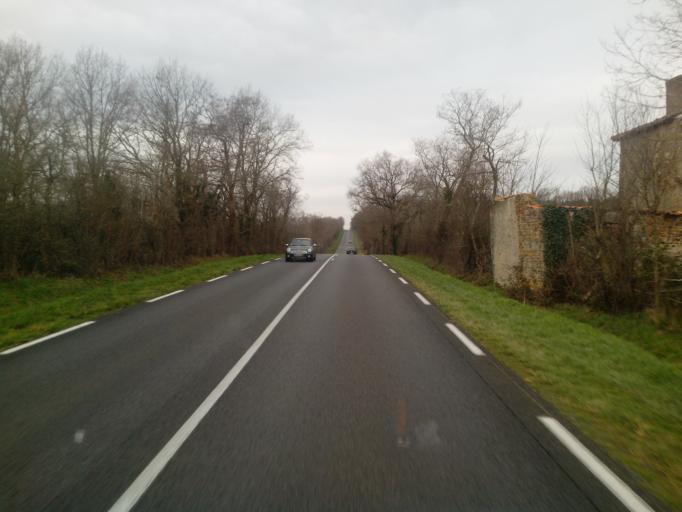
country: FR
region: Poitou-Charentes
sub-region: Departement de la Vienne
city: Lussac-les-Chateaux
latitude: 46.3494
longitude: 0.7894
